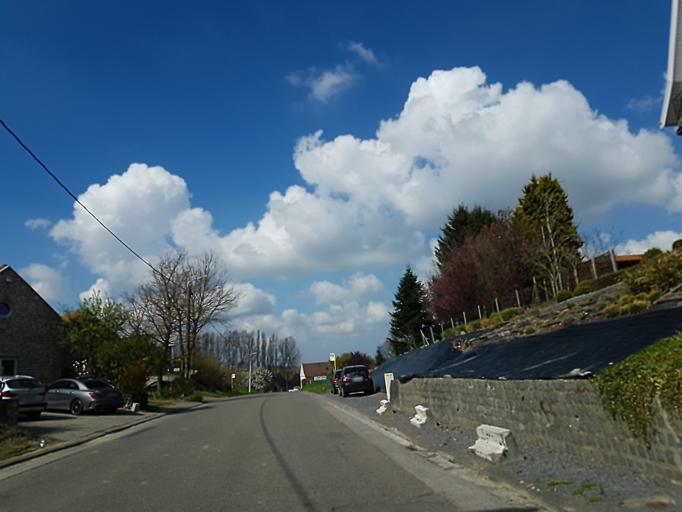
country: BE
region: Flanders
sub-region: Provincie Vlaams-Brabant
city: Gooik
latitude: 50.8185
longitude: 4.1213
